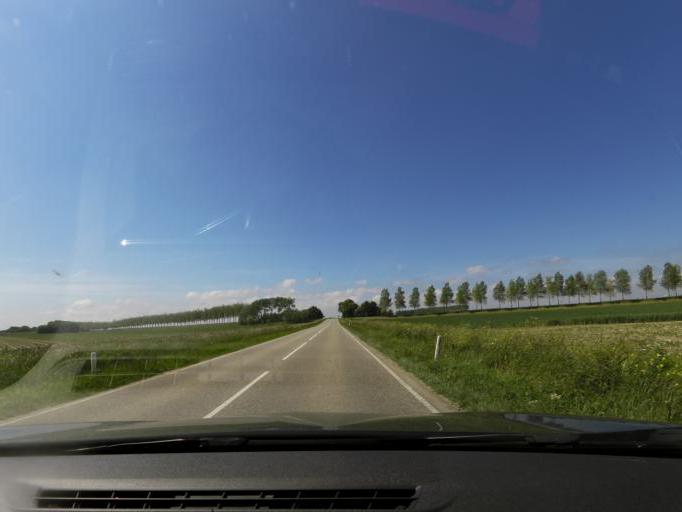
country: NL
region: South Holland
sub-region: Gemeente Goeree-Overflakkee
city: Dirksland
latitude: 51.7794
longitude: 4.0741
